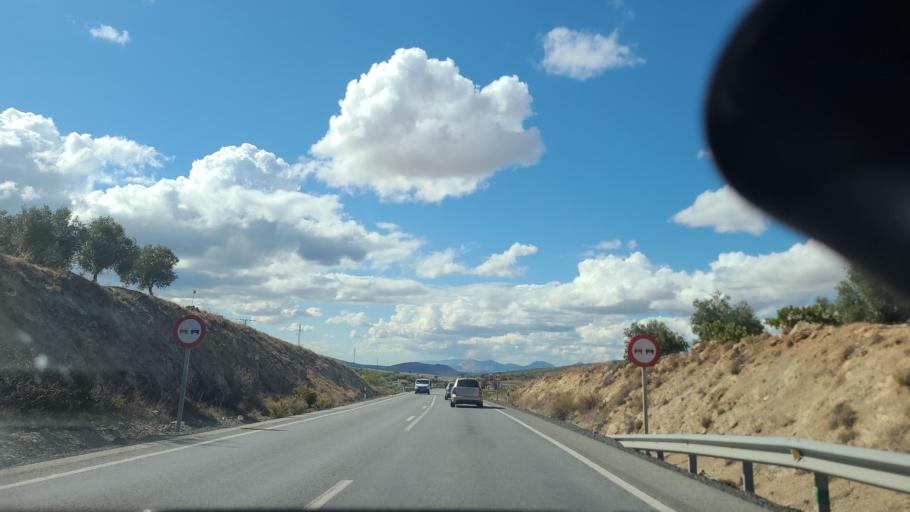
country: ES
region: Andalusia
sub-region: Provincia de Granada
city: Pinar
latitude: 37.4068
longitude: -3.3775
